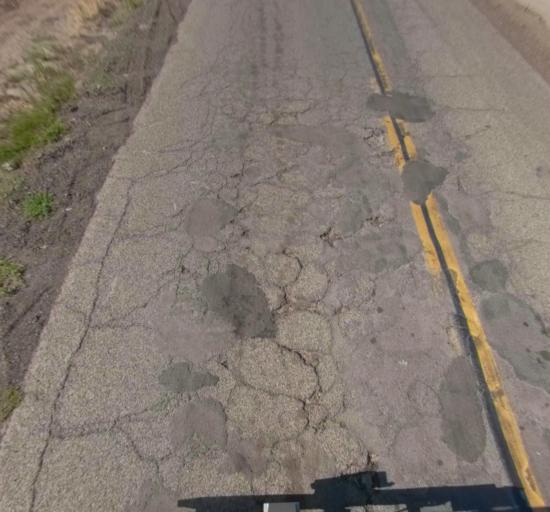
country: US
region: California
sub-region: Madera County
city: Parkwood
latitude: 36.8661
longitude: -120.1284
